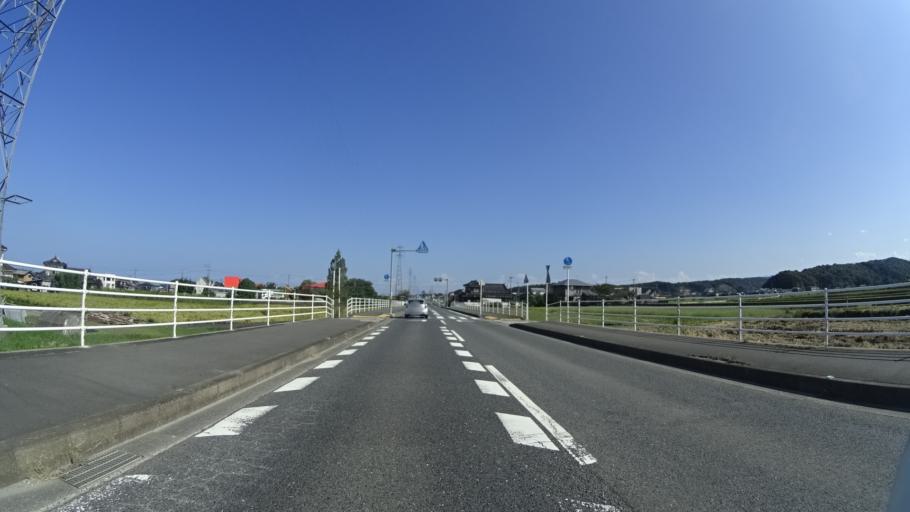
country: JP
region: Fukuoka
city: Shiida
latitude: 33.6495
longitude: 131.0537
